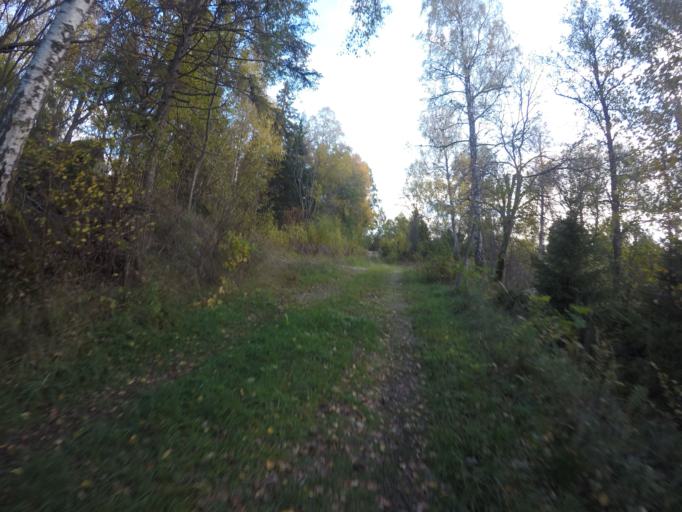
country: SE
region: Vaestmanland
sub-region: Arboga Kommun
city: Tyringe
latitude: 59.3220
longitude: 15.9738
